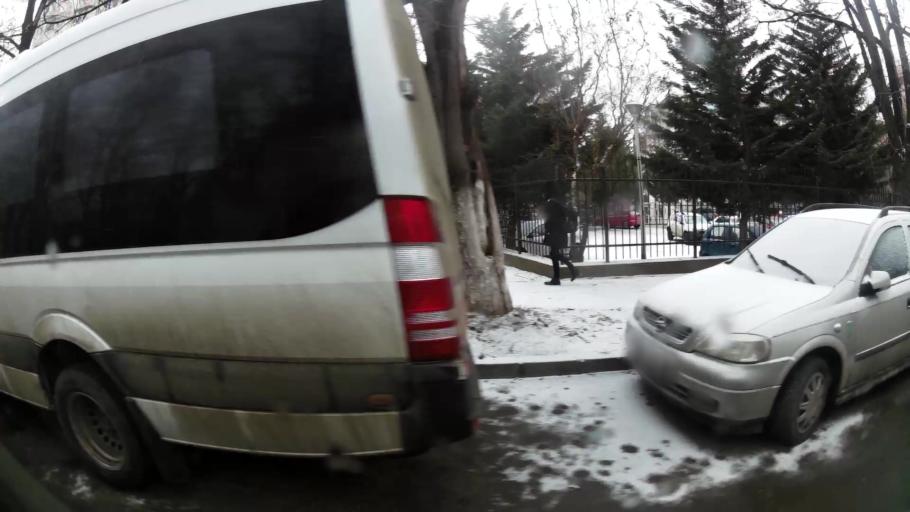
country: RO
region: Prahova
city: Ploiesti
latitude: 44.9535
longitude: 26.0111
